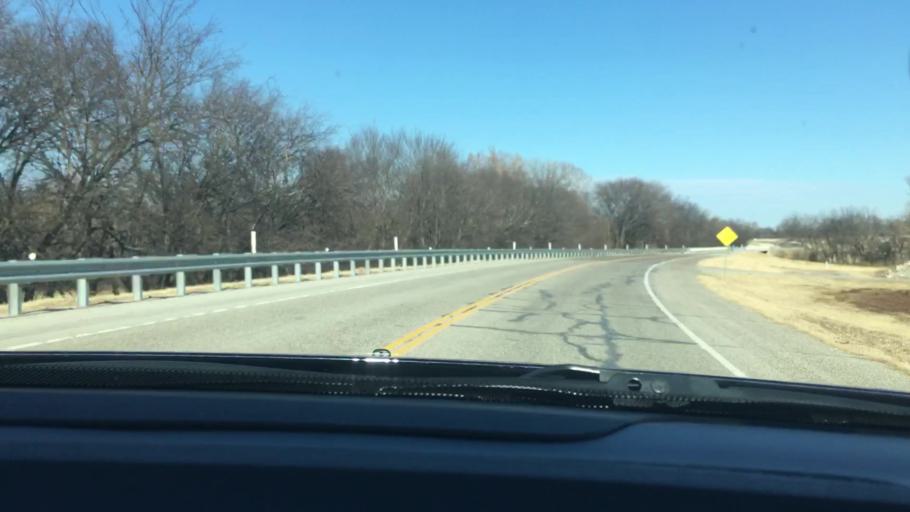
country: US
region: Oklahoma
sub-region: Murray County
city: Davis
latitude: 34.5118
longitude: -97.1226
